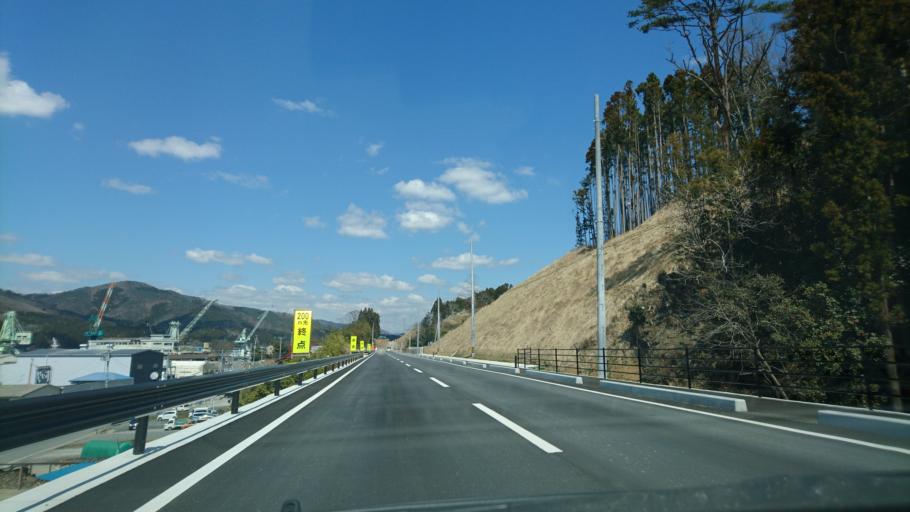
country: JP
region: Iwate
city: Ofunato
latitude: 38.9053
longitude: 141.5893
